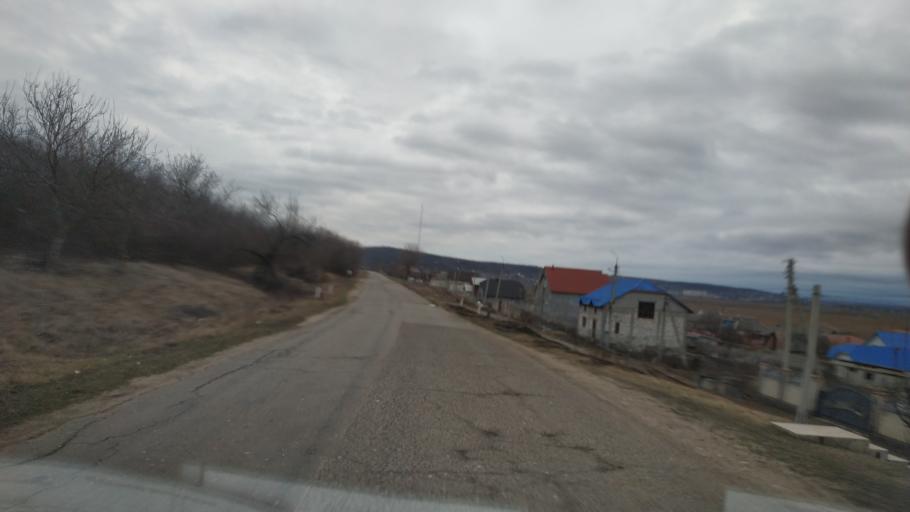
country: MD
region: Causeni
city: Causeni
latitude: 46.6625
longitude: 29.4489
